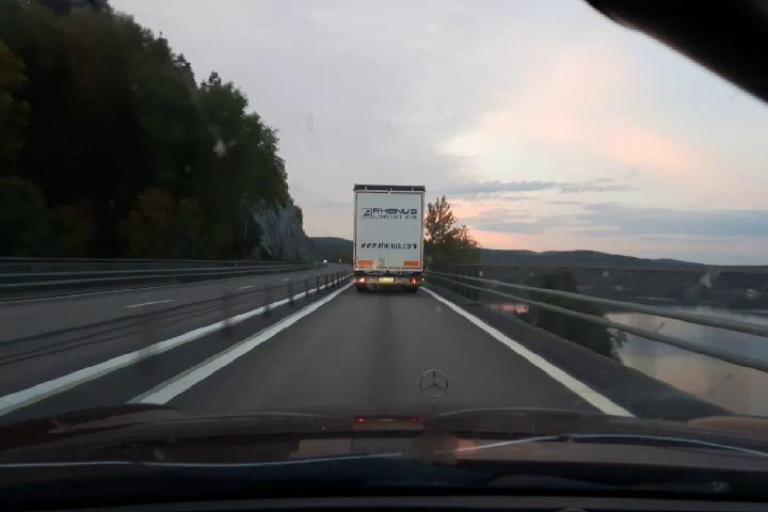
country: SE
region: Vaesternorrland
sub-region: Haernoesands Kommun
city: Haernoesand
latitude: 62.8255
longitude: 17.9695
